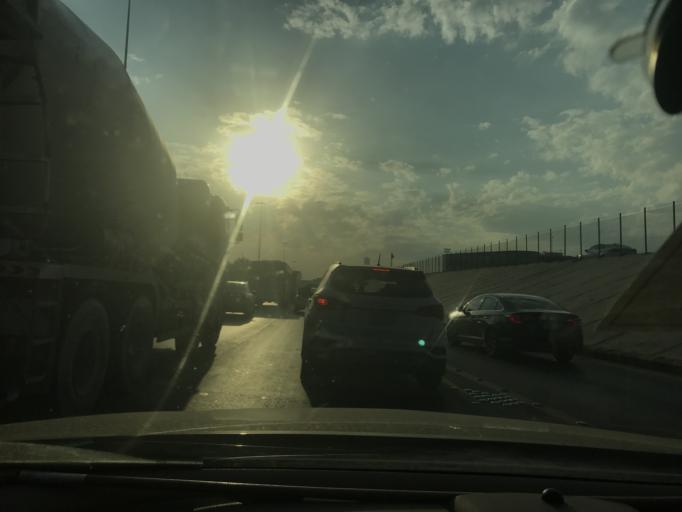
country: SA
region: Ar Riyad
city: Riyadh
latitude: 24.7809
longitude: 46.6933
